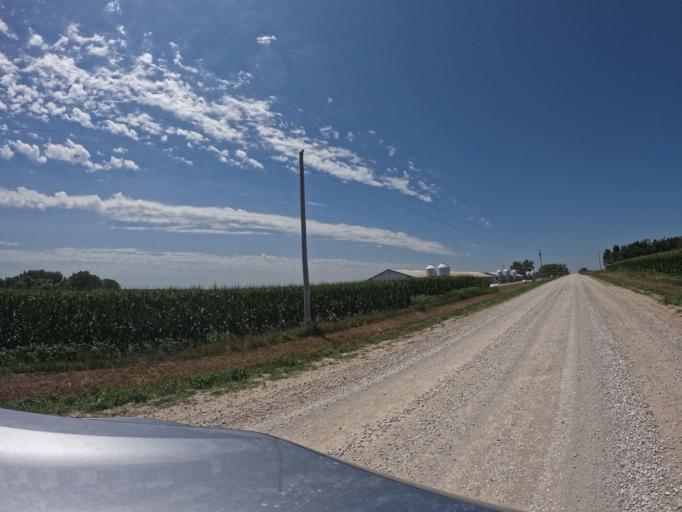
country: US
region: Iowa
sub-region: Keokuk County
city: Sigourney
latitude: 41.4667
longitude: -92.3602
